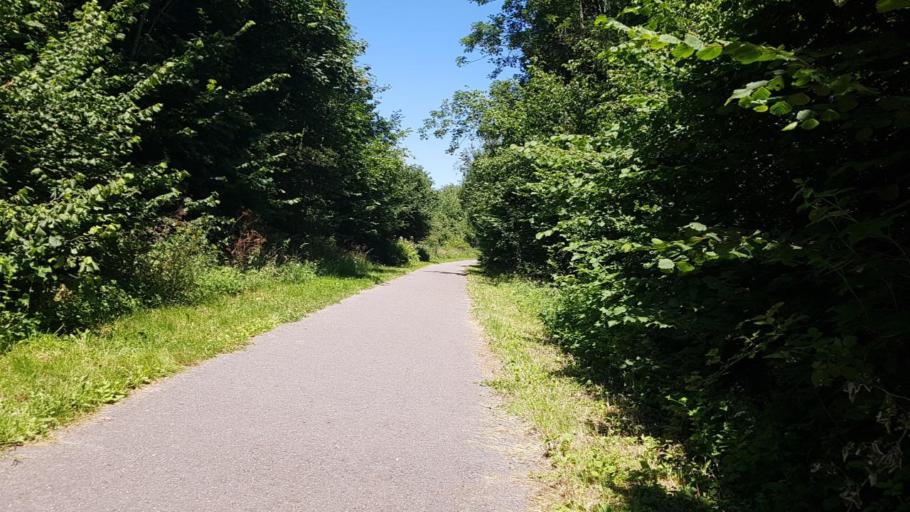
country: BE
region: Wallonia
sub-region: Province du Hainaut
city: Beaumont
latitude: 50.2353
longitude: 4.2426
